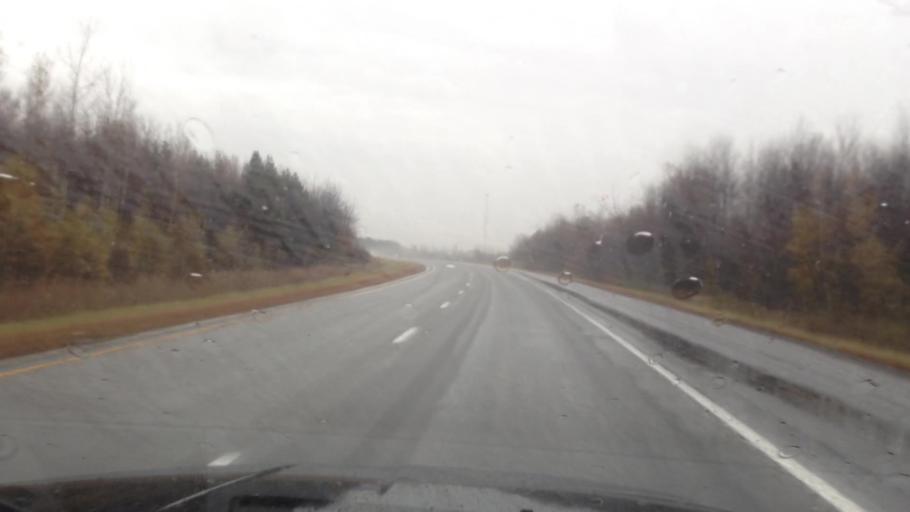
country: CA
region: Ontario
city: Casselman
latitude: 45.3040
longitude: -75.1419
